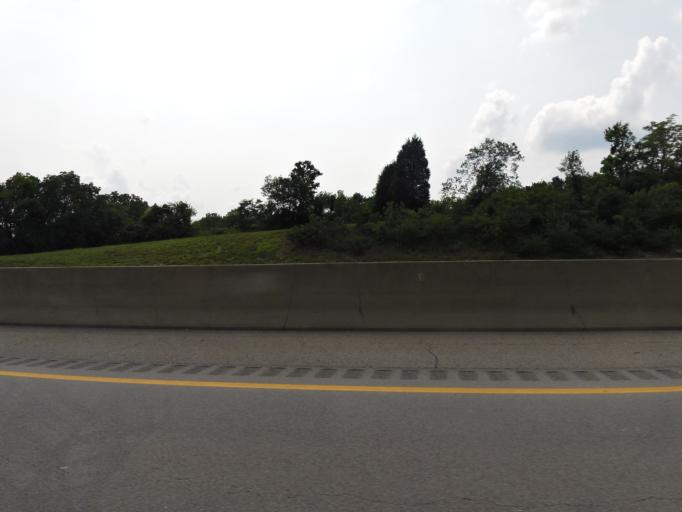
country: US
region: Kentucky
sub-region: Boone County
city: Walton
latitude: 38.8945
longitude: -84.6267
